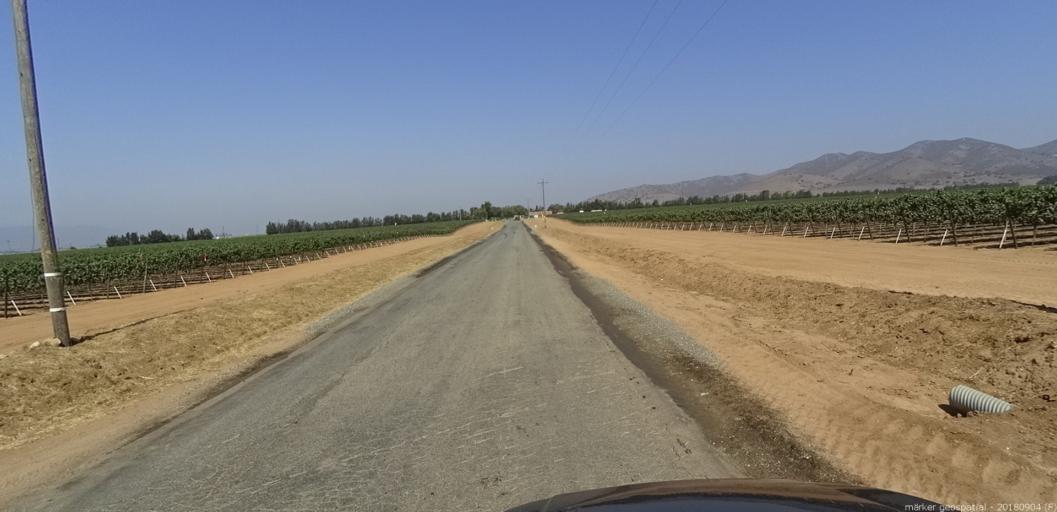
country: US
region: California
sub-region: Monterey County
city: Gonzales
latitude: 36.5462
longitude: -121.4327
